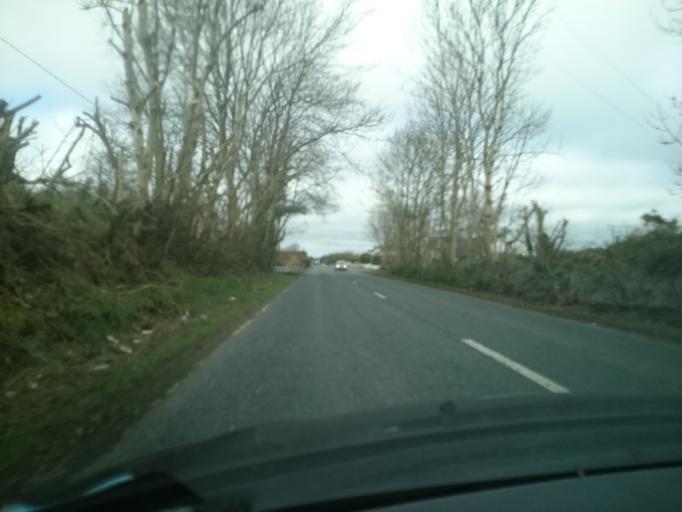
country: IE
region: Connaught
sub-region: Maigh Eo
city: Claremorris
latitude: 53.7496
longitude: -9.0267
